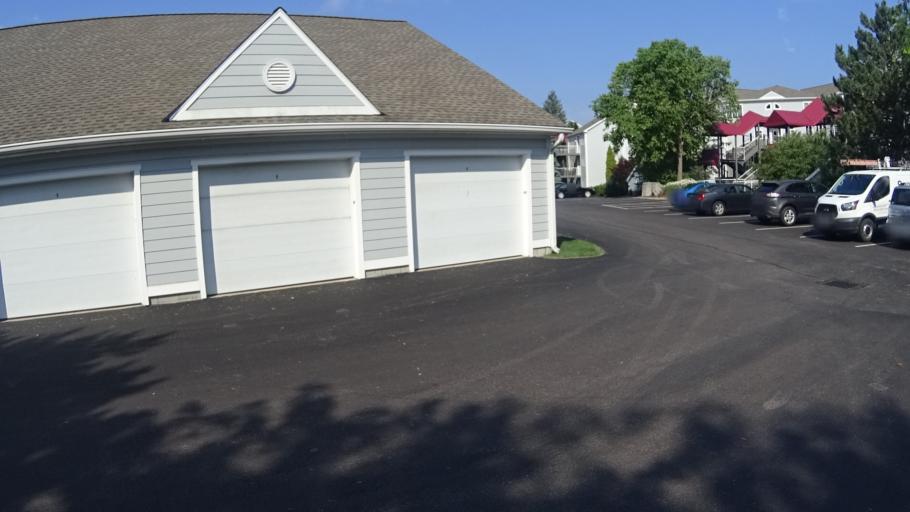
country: US
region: Ohio
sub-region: Lorain County
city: Vermilion
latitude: 41.3938
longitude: -82.4377
